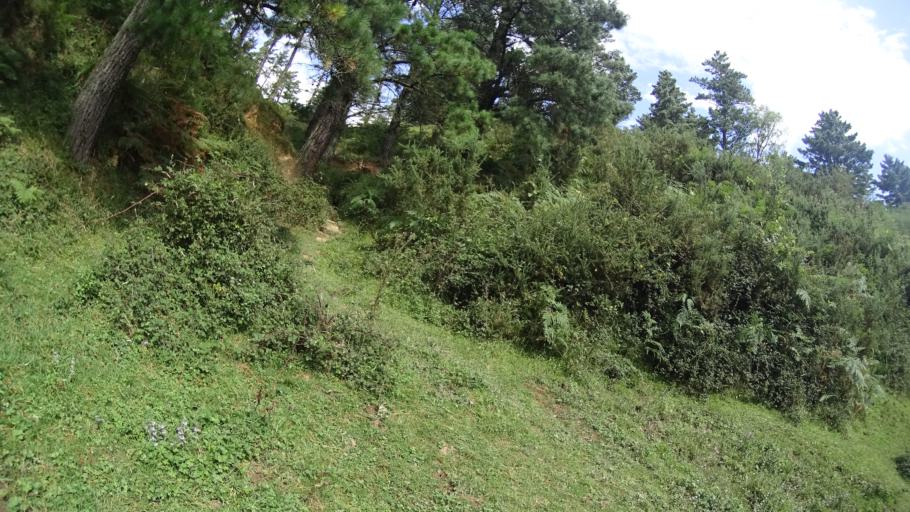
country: ES
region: Basque Country
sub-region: Bizkaia
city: Urtuella
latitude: 43.2828
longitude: -3.0728
